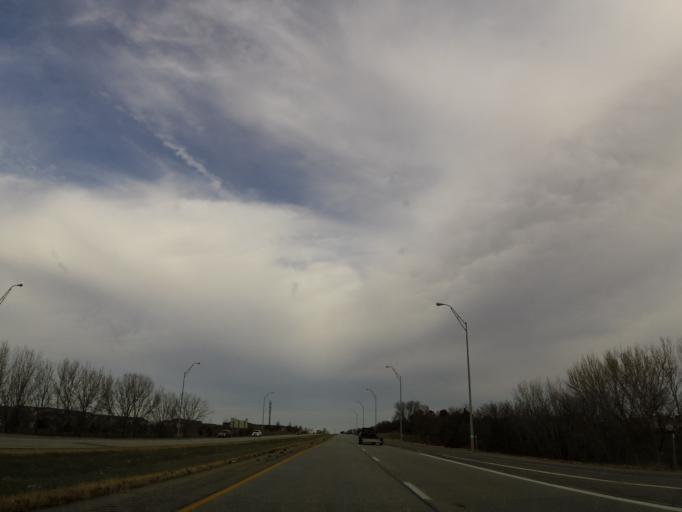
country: US
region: Iowa
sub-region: Scott County
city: Bettendorf
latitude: 41.5785
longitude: -90.5220
